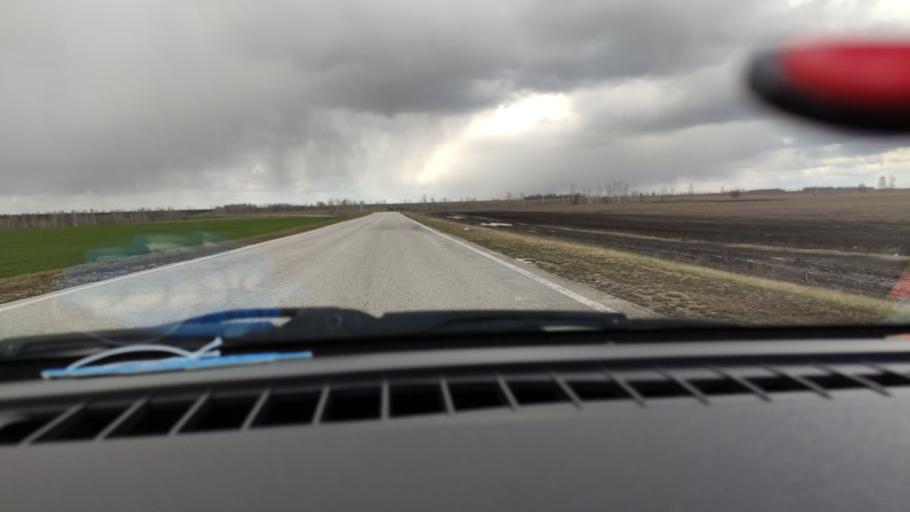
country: RU
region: Samara
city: Povolzhskiy
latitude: 53.7933
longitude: 49.7258
